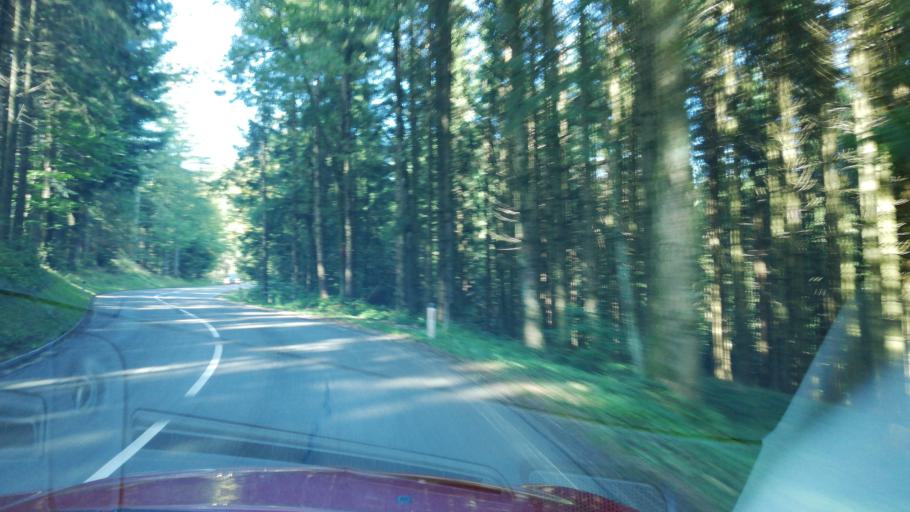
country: AT
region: Upper Austria
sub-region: Politischer Bezirk Vocklabruck
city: Redleiten
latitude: 48.1053
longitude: 13.5664
